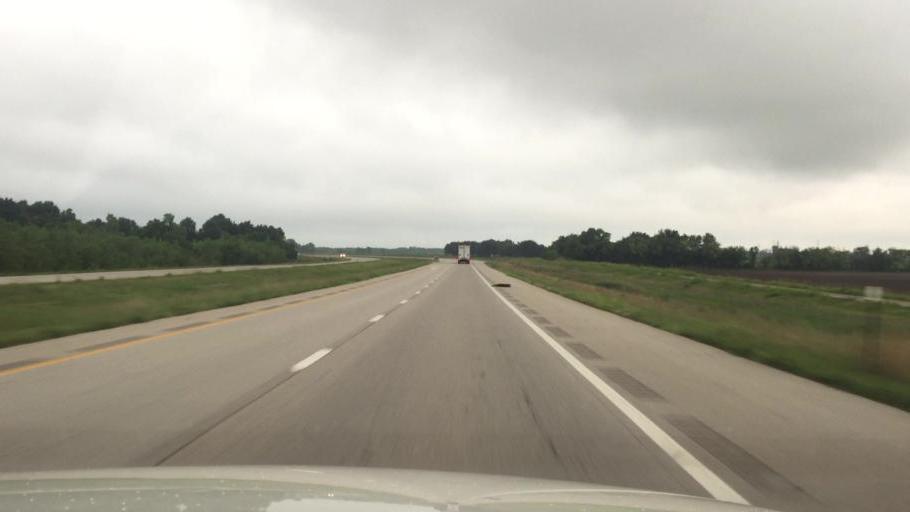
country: US
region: Kansas
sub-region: Montgomery County
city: Coffeyville
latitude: 37.0826
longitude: -95.5899
